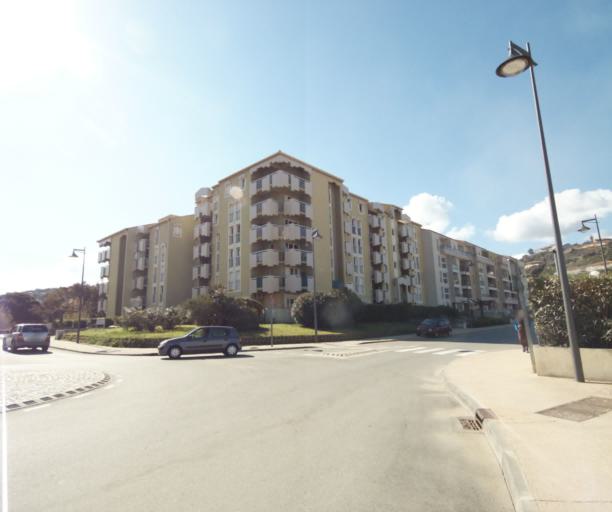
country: FR
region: Corsica
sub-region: Departement de la Corse-du-Sud
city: Propriano
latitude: 41.6739
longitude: 8.9017
